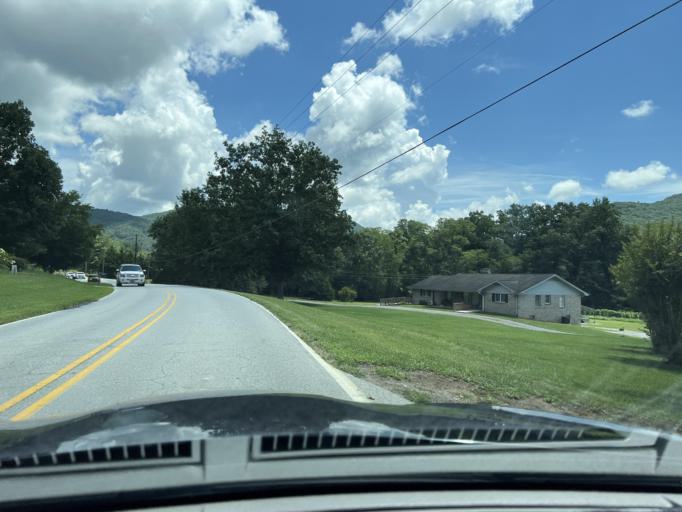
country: US
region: North Carolina
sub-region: Henderson County
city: Hoopers Creek
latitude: 35.4380
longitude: -82.4443
